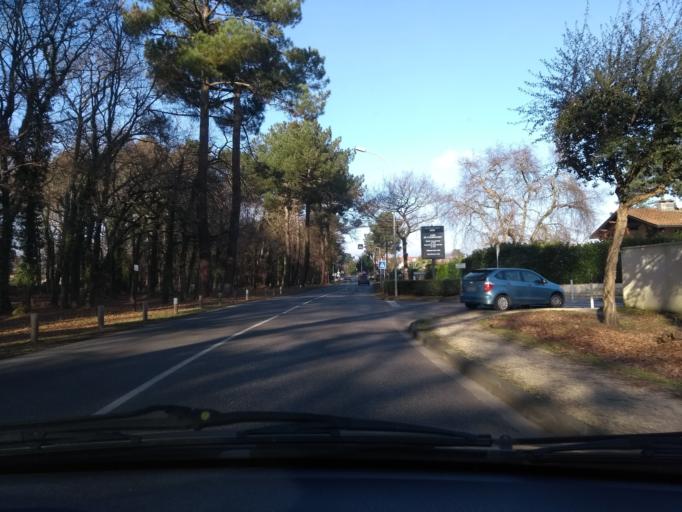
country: FR
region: Aquitaine
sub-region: Departement de la Gironde
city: Gujan-Mestras
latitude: 44.6196
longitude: -1.0733
